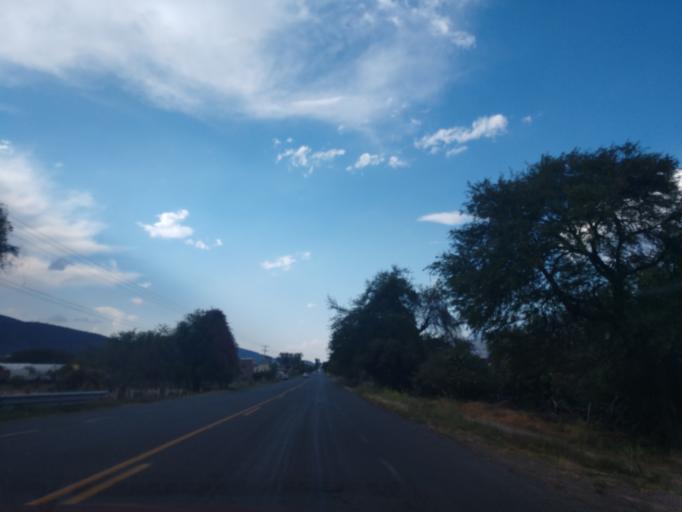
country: MX
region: Jalisco
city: Jocotepec
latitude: 20.2316
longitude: -103.4205
